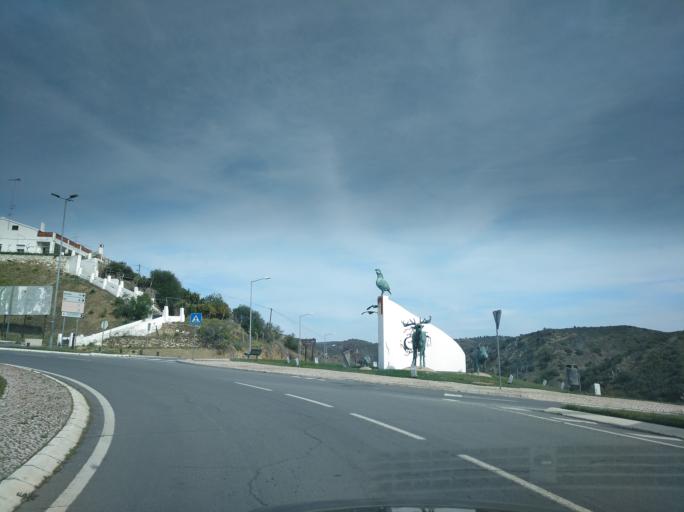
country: PT
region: Beja
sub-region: Mertola
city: Mertola
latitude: 37.6417
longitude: -7.6583
